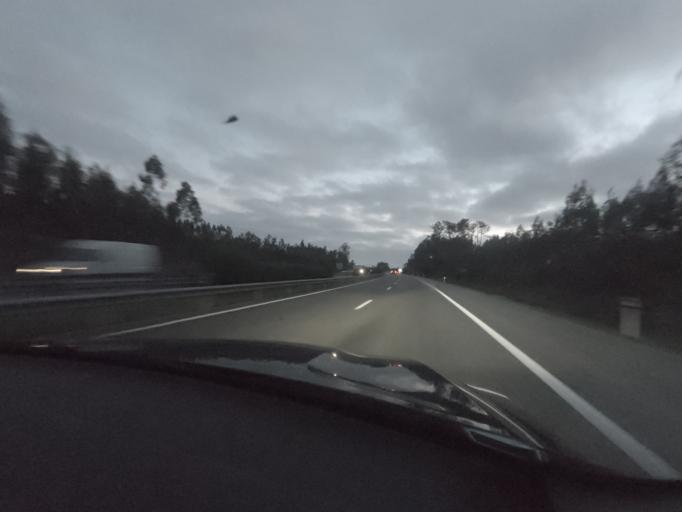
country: PT
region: Leiria
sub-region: Pombal
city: Pombal
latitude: 39.9539
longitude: -8.6694
